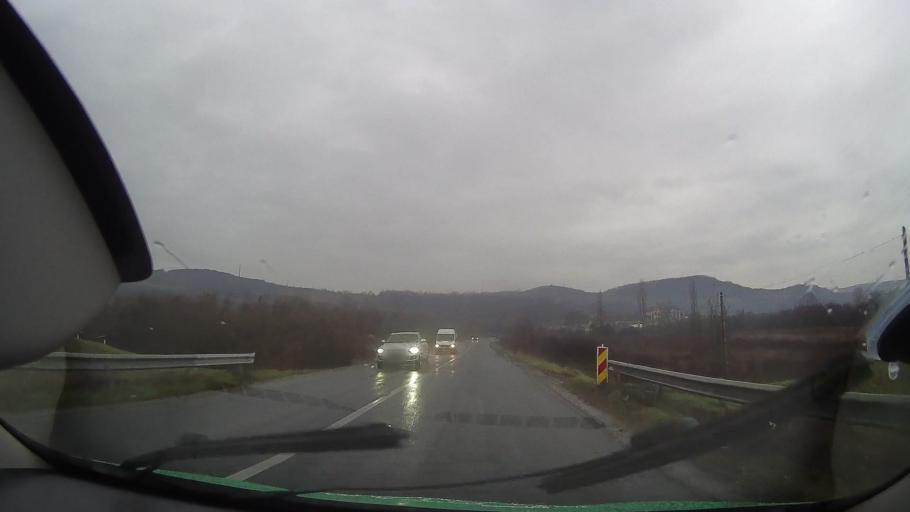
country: RO
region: Bihor
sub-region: Comuna Sambata
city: Sambata
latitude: 46.7925
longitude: 22.2039
